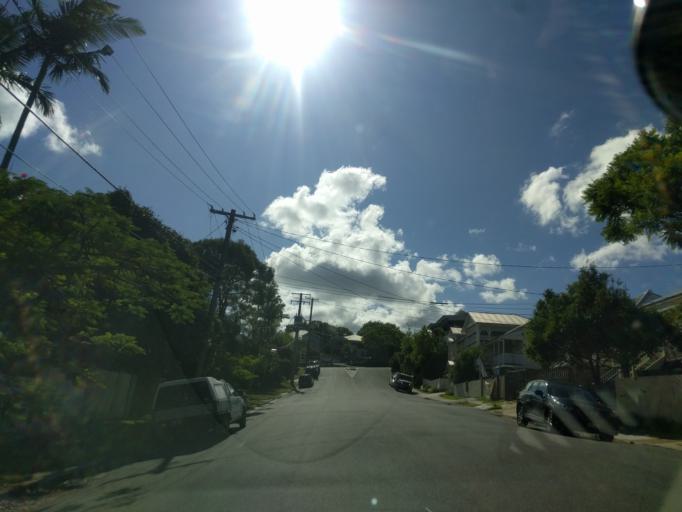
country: AU
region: Queensland
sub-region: Brisbane
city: Milton
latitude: -27.4603
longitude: 152.9954
